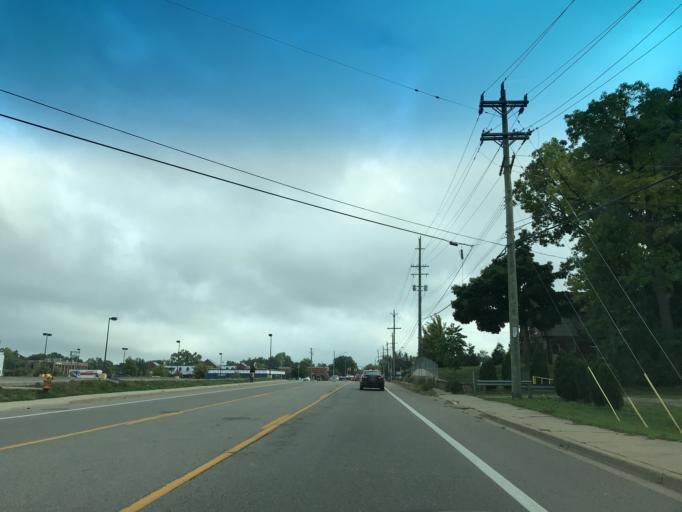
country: US
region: Michigan
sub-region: Washtenaw County
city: Ypsilanti
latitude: 42.2525
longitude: -83.6611
